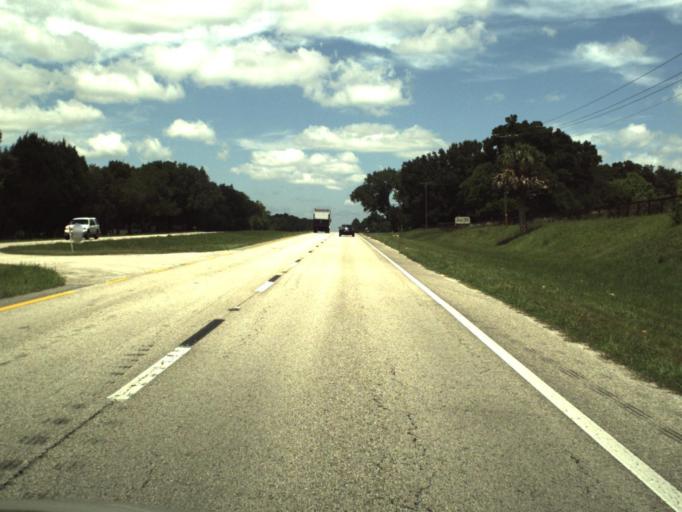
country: US
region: Florida
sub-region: Marion County
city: Citra
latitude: 29.3499
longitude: -82.1591
